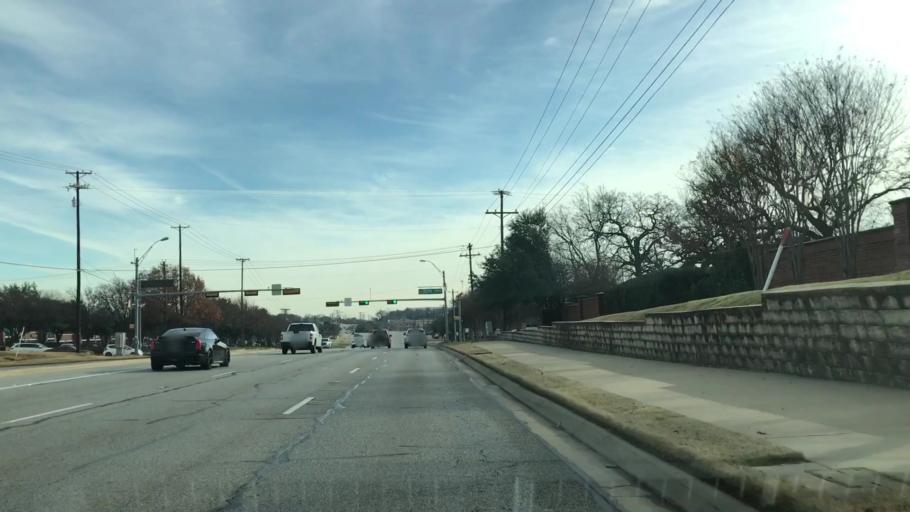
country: US
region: Texas
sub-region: Tarrant County
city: Southlake
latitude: 32.9410
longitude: -97.1603
